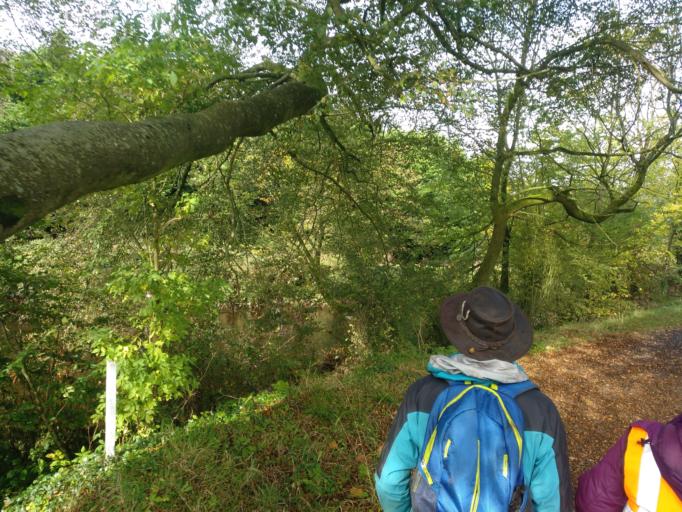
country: IE
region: Leinster
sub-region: Kilkenny
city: Castlecomer
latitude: 52.8016
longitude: -7.2092
